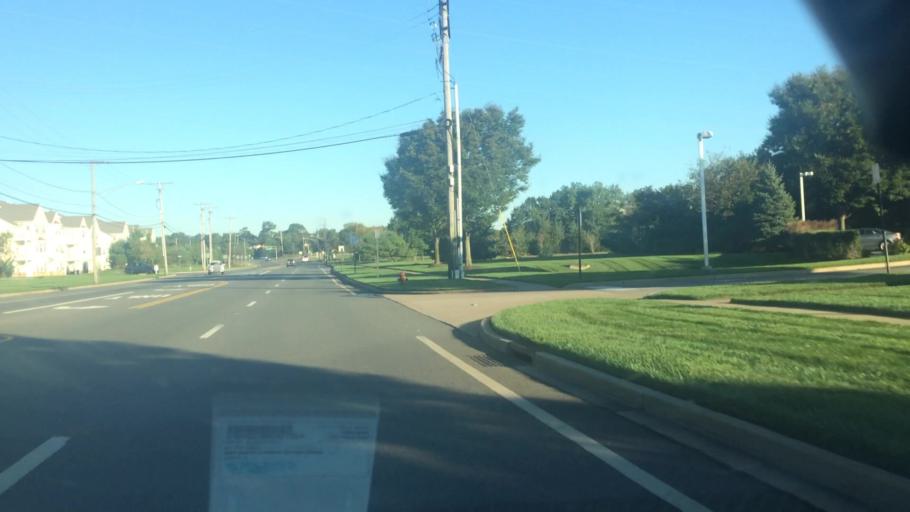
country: US
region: New Jersey
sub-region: Ocean County
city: Silver Ridge
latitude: 39.9880
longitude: -74.2015
